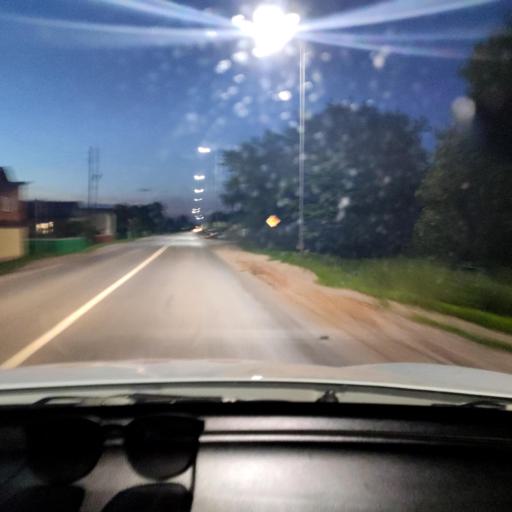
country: RU
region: Tatarstan
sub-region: Alekseyevskiy Rayon
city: Alekseyevskoye
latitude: 55.4260
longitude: 49.8854
